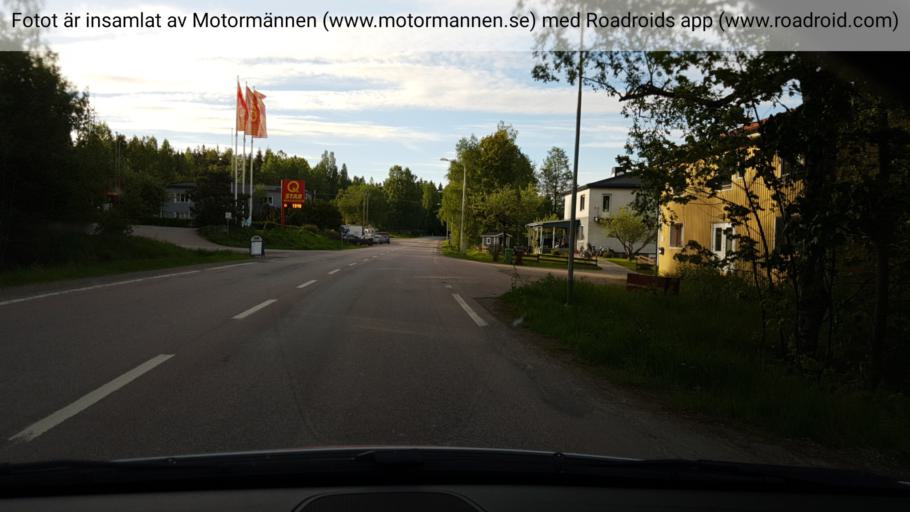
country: SE
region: Vaestmanland
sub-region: Skinnskattebergs Kommun
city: Skinnskatteberg
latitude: 59.8302
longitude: 15.6772
